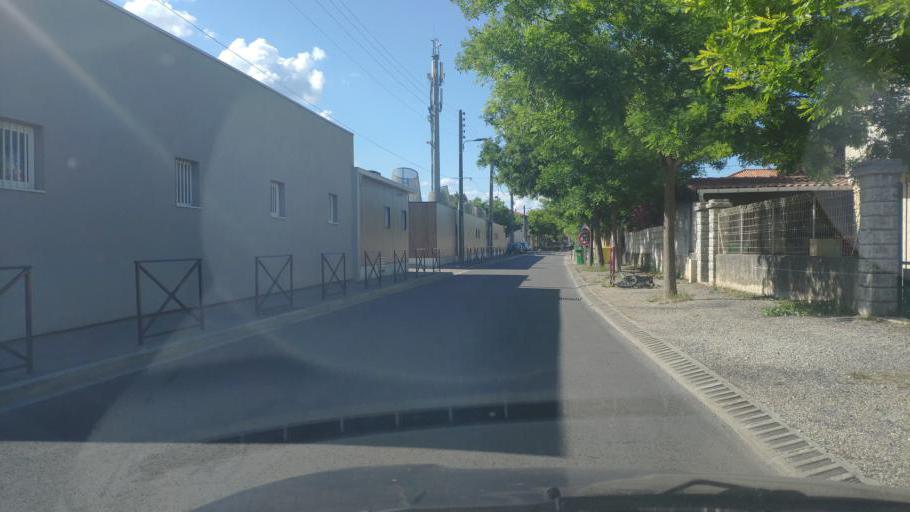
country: FR
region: Provence-Alpes-Cote d'Azur
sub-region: Departement du Vaucluse
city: Entraigues-sur-la-Sorgue
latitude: 43.9996
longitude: 4.9277
